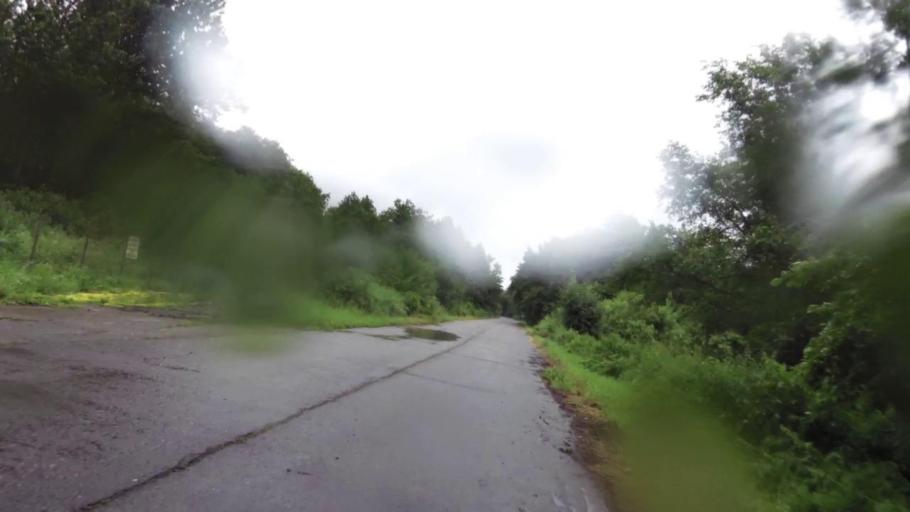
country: PL
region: West Pomeranian Voivodeship
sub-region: Powiat kolobrzeski
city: Ustronie Morskie
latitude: 54.2273
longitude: 15.8044
